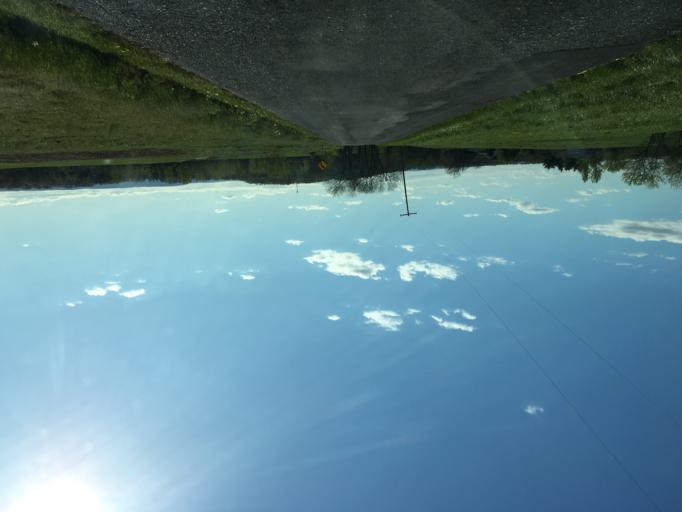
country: US
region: Maryland
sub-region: Frederick County
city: Emmitsburg
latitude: 39.6446
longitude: -77.2947
